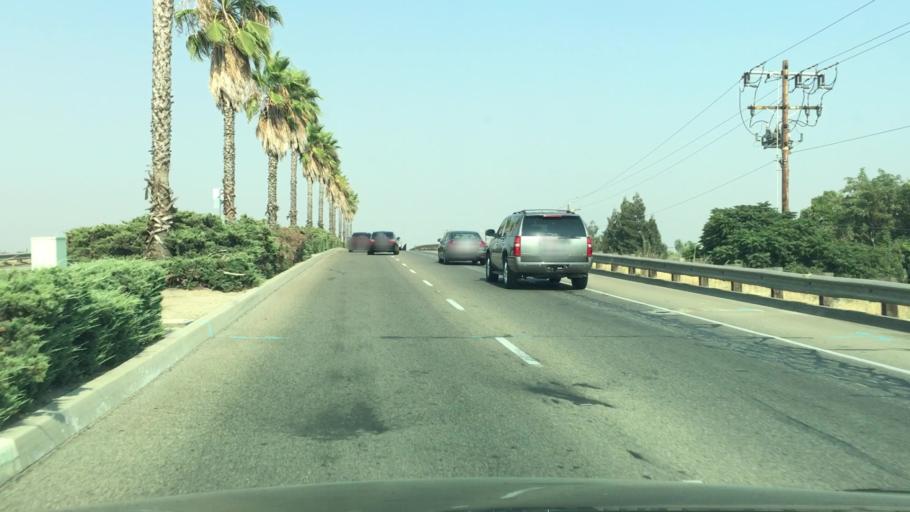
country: US
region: California
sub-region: Fresno County
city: West Park
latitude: 36.8370
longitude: -119.8880
